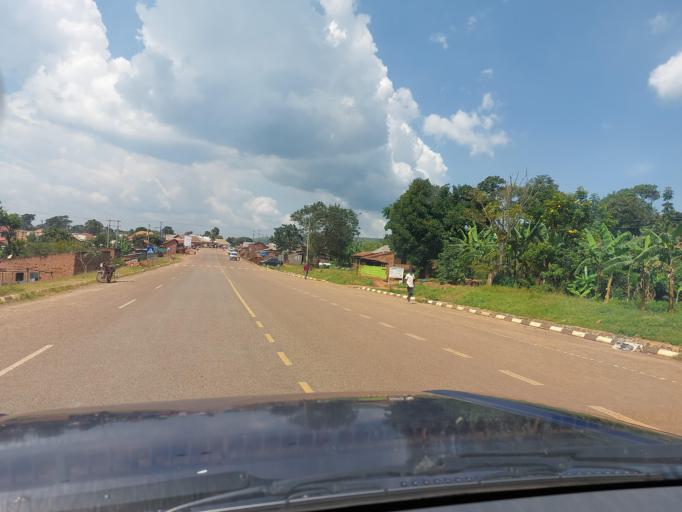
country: UG
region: Central Region
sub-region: Buikwe District
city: Buikwe
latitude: 0.3104
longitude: 33.1006
